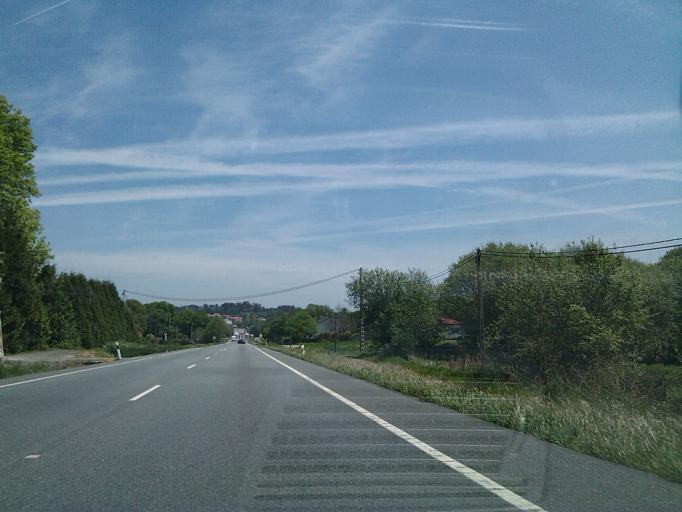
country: ES
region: Galicia
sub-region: Provincia da Coruna
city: Curtis
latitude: 43.1307
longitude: -8.0460
